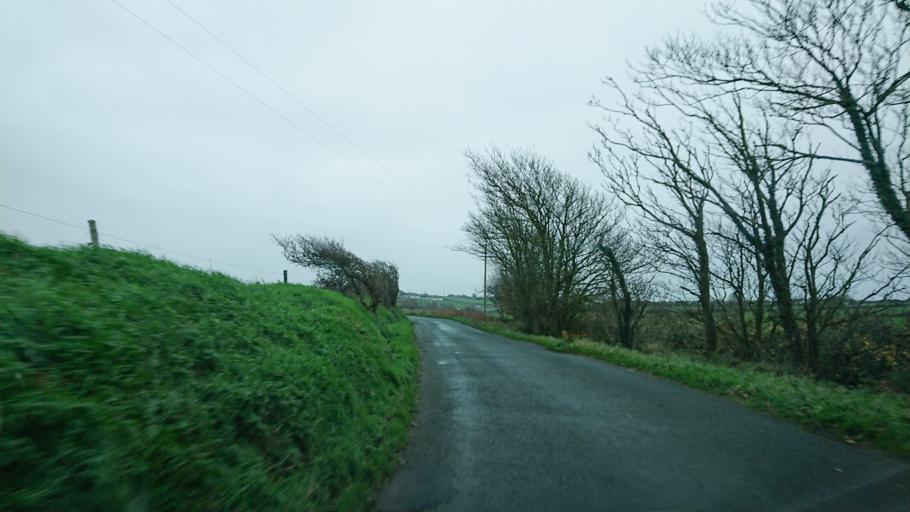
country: IE
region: Munster
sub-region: Waterford
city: Dunmore East
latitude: 52.1486
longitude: -7.0584
